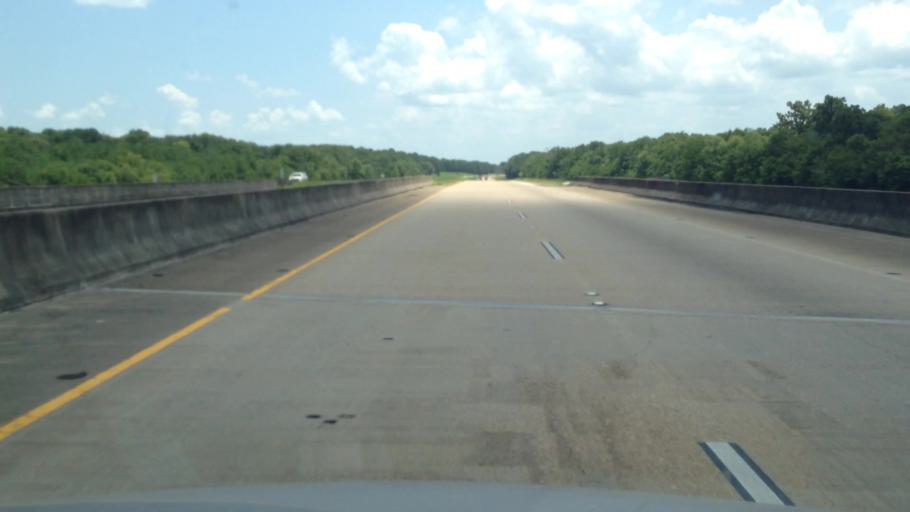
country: US
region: Louisiana
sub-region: Rapides Parish
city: Woodworth
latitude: 31.1646
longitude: -92.4600
